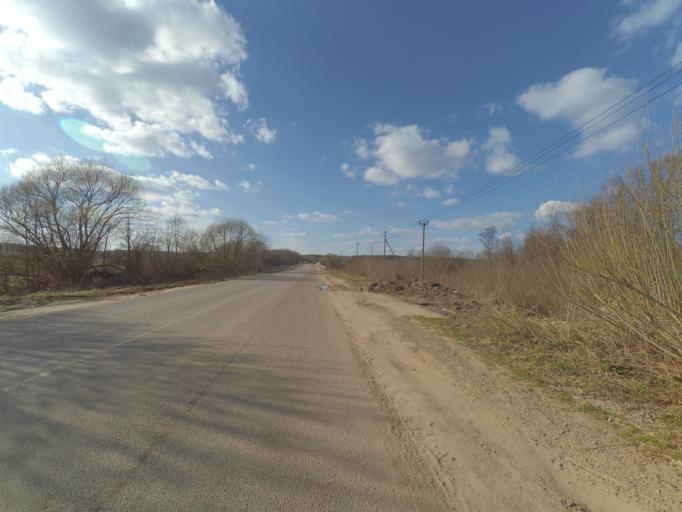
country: RU
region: Moskovskaya
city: Bol'shoye Gryzlovo
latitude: 54.8875
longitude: 37.7983
